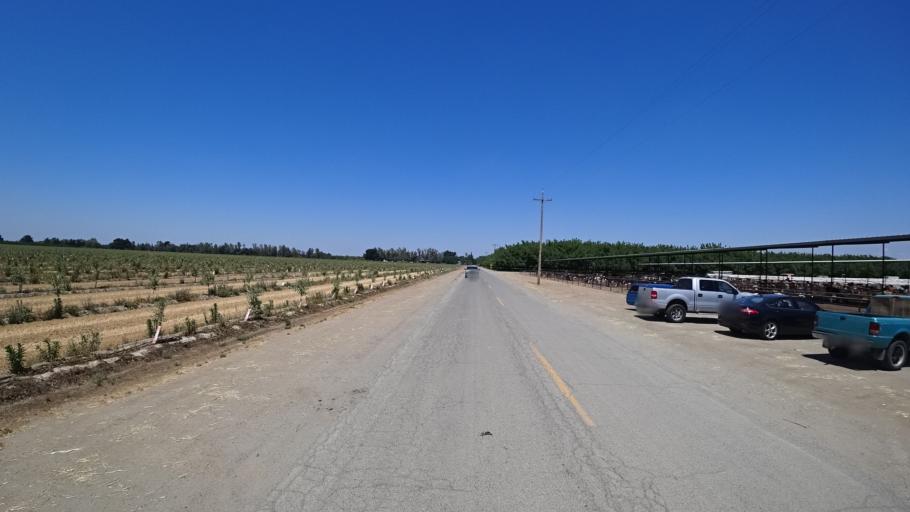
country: US
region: California
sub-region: Kings County
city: Lucerne
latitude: 36.4274
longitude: -119.6010
